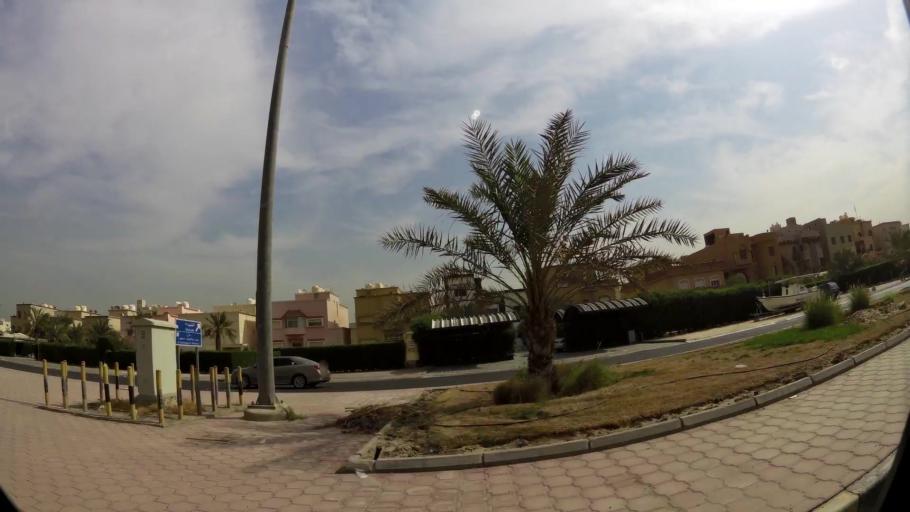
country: KW
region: Mubarak al Kabir
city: Sabah as Salim
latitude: 29.2698
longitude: 48.0222
